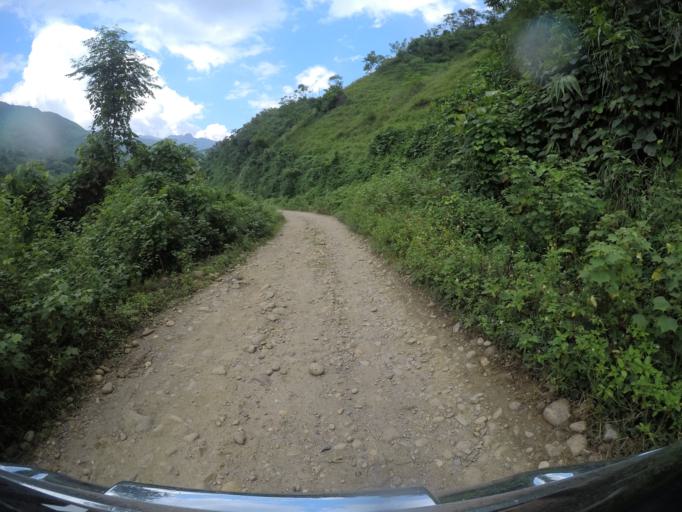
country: VN
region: Yen Bai
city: Son Thinh
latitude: 21.6674
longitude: 104.5175
